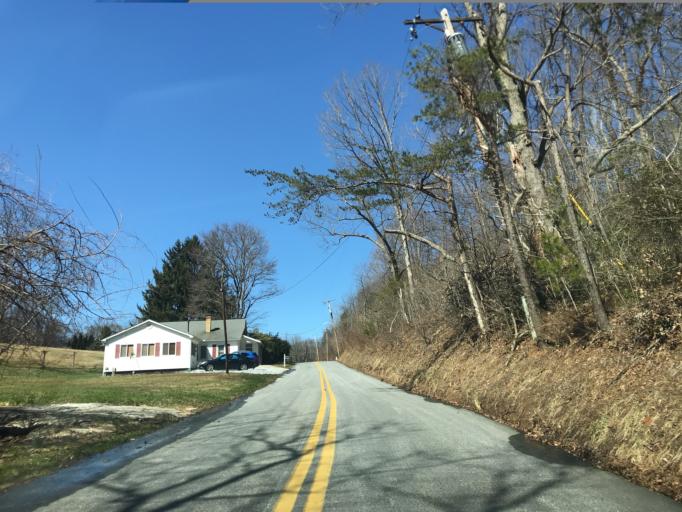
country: US
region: Pennsylvania
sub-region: York County
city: New Freedom
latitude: 39.6780
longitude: -76.6824
